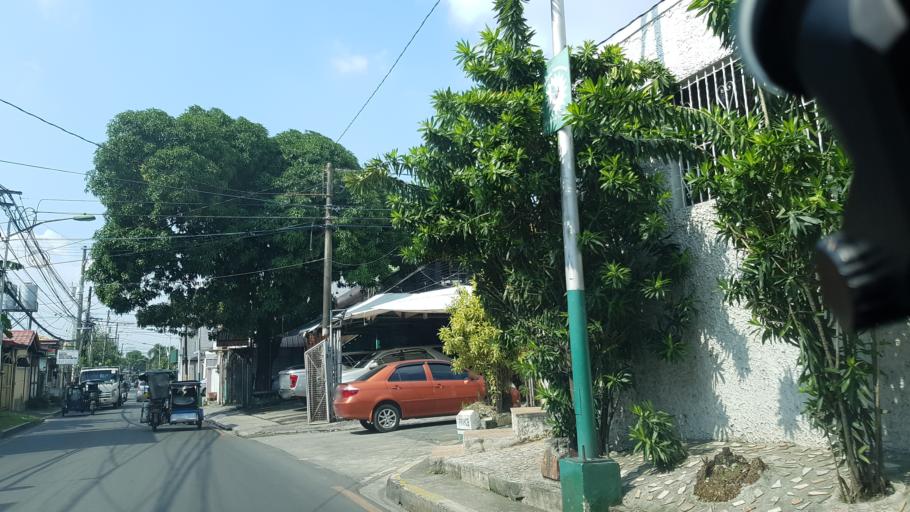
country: PH
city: Sambayanihan People's Village
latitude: 14.4786
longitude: 121.0308
